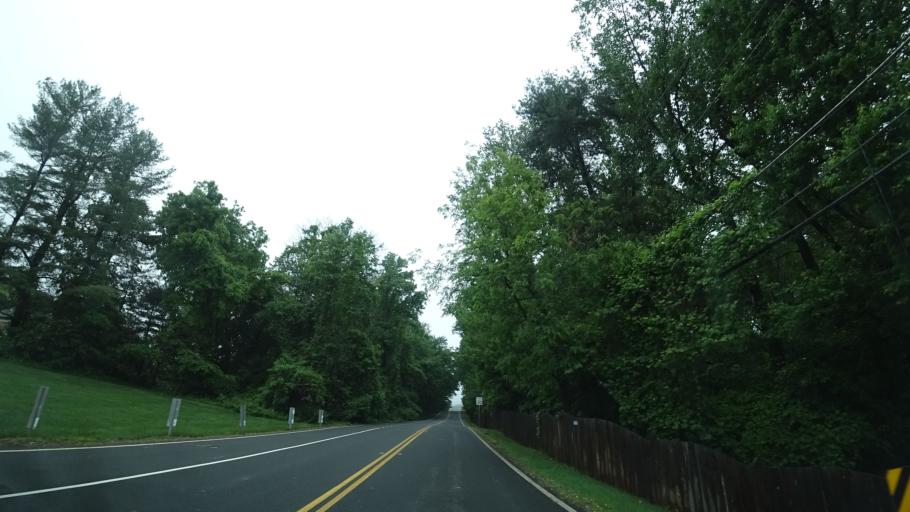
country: US
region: Maryland
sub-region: Montgomery County
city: Brookmont
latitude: 38.9367
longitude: -77.1287
